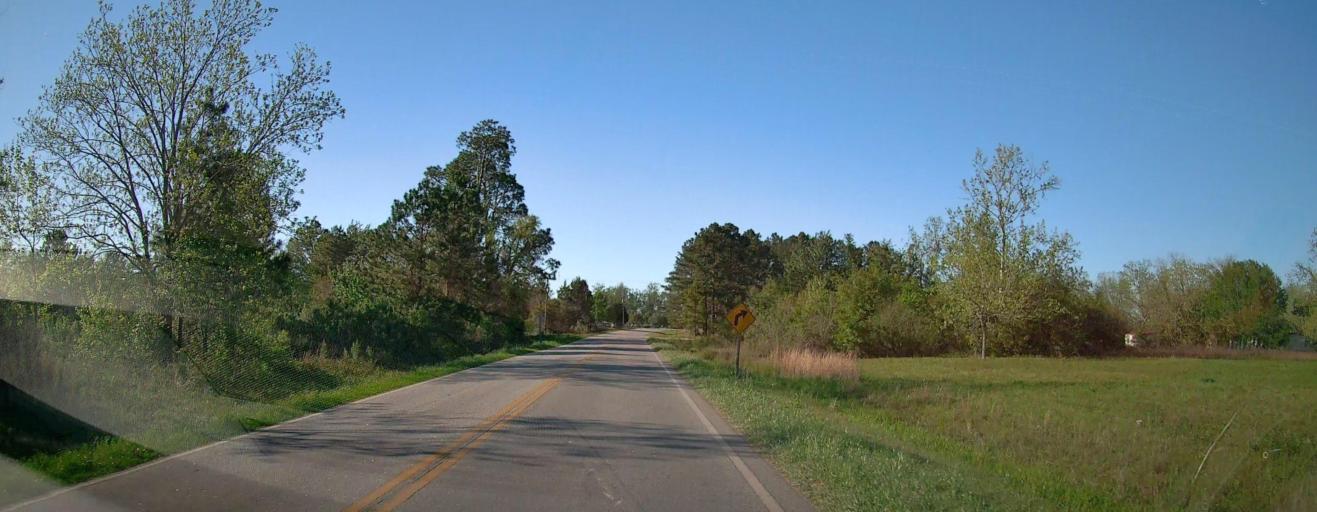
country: US
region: Georgia
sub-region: Ben Hill County
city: Fitzgerald
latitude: 31.7332
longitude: -83.2351
